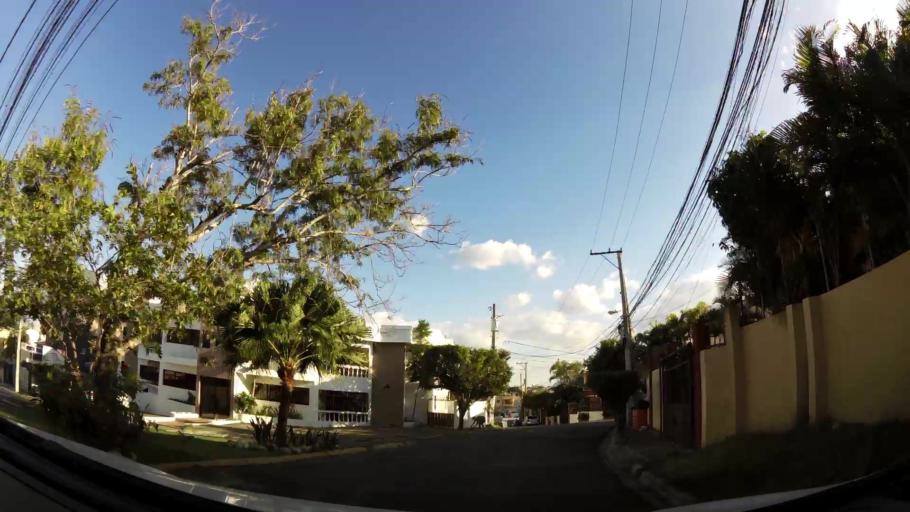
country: DO
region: Nacional
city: Santo Domingo
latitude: 18.4926
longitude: -69.9723
